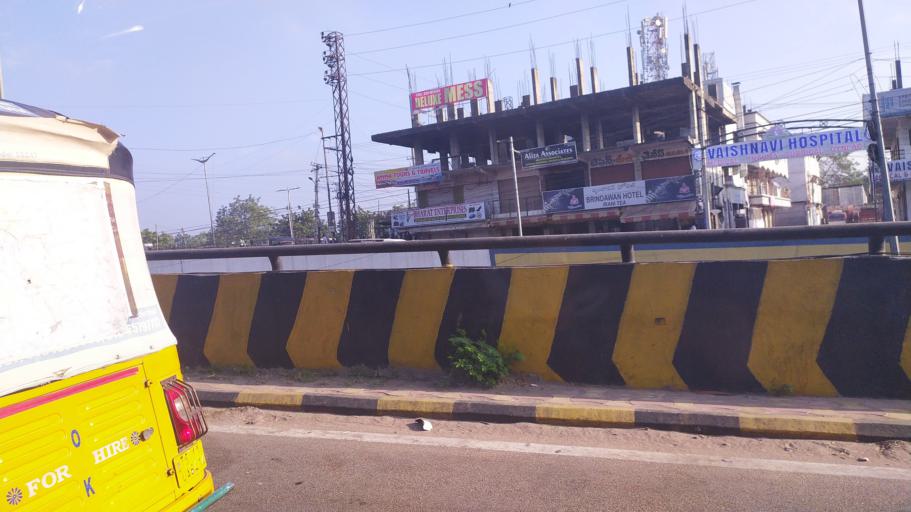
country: IN
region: Telangana
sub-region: Hyderabad
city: Hyderabad
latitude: 17.3212
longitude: 78.4324
